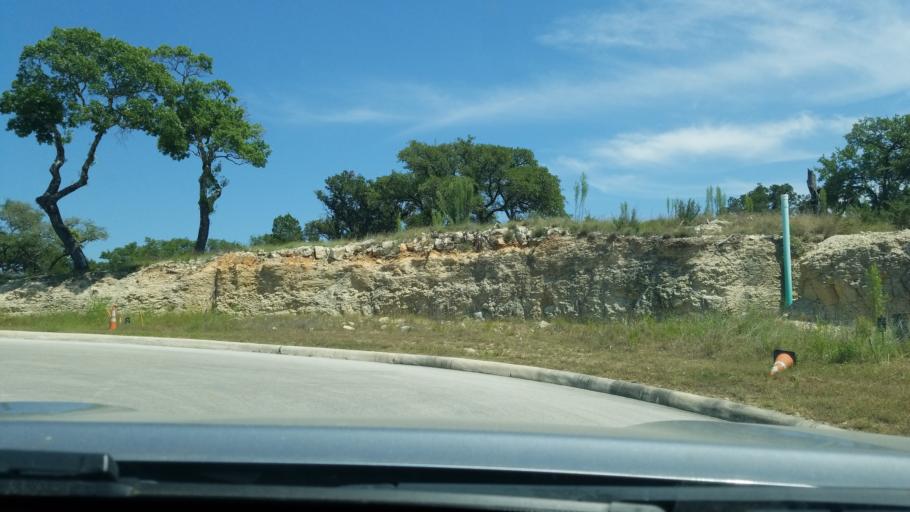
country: US
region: Texas
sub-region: Kendall County
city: Boerne
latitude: 29.7943
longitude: -98.6924
